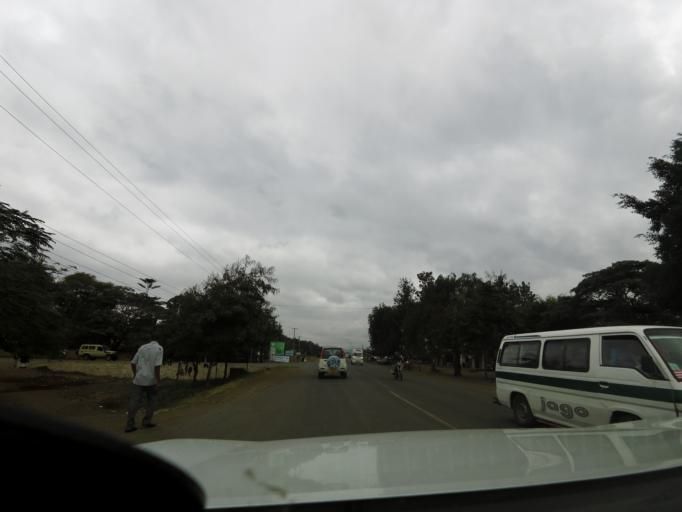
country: TZ
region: Arusha
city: Arusha
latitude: -3.3612
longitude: 36.6605
